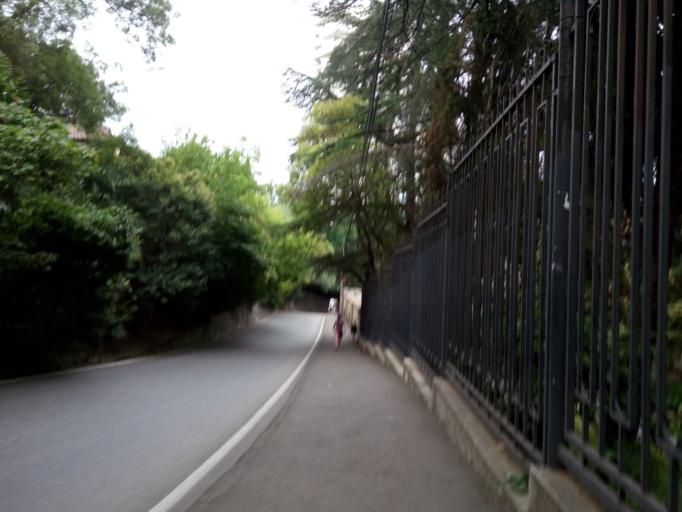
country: RU
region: Krasnodarskiy
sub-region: Sochi City
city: Sochi
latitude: 43.5643
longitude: 39.7603
